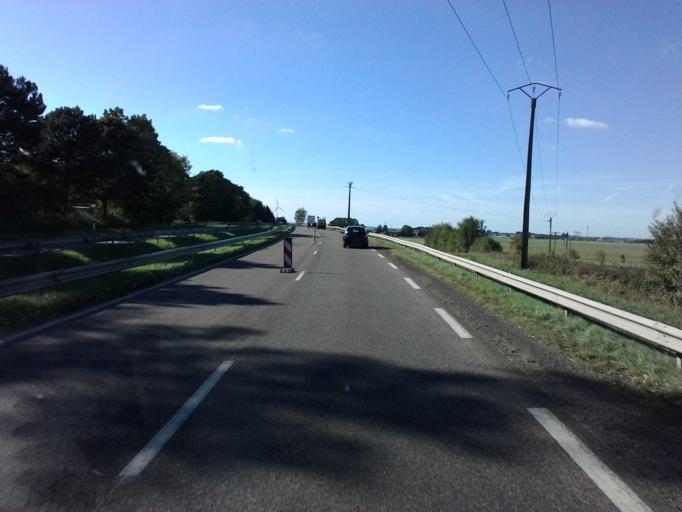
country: FR
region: Lorraine
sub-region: Departement de Meurthe-et-Moselle
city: Villers-la-Montagne
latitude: 49.4756
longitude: 5.8307
